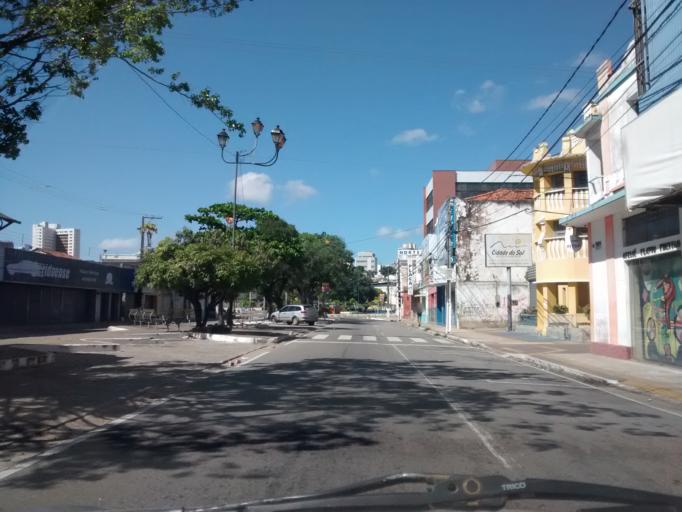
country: BR
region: Rio Grande do Norte
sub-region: Natal
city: Natal
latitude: -5.7782
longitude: -35.2049
